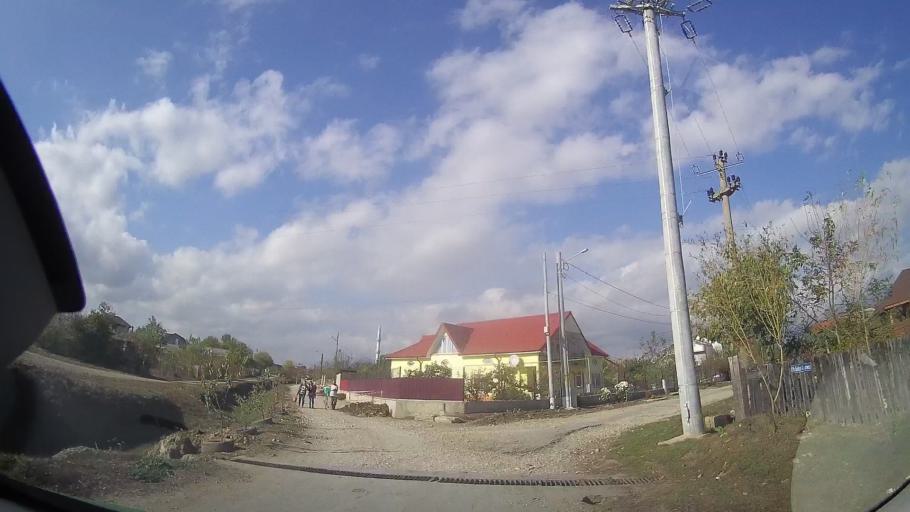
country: RO
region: Constanta
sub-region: Comuna Douazeci si Trei August
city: Douazeci si Trei August
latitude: 43.9128
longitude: 28.5867
